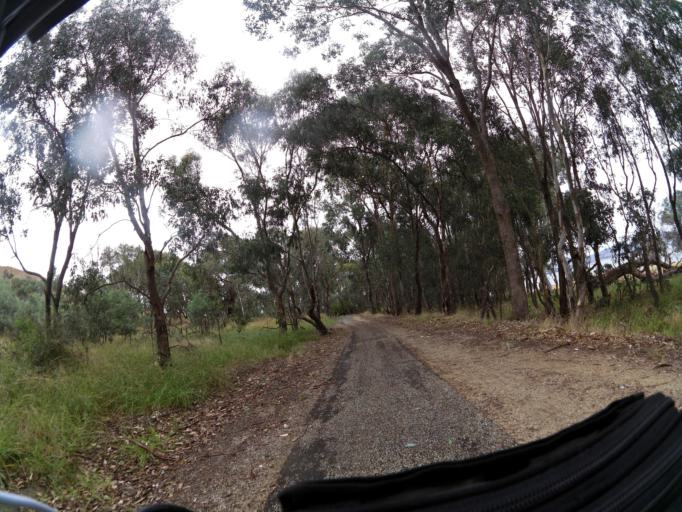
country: AU
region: New South Wales
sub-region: Albury Municipality
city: East Albury
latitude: -36.2235
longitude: 147.1094
